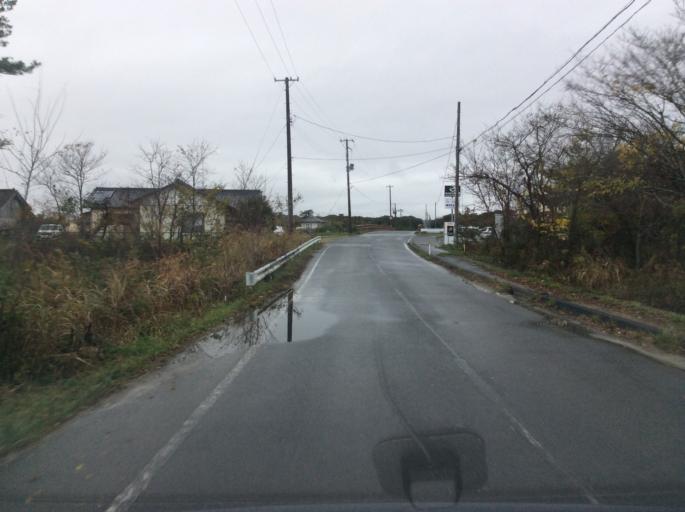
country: JP
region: Fukushima
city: Iwaki
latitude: 37.0663
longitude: 140.9743
